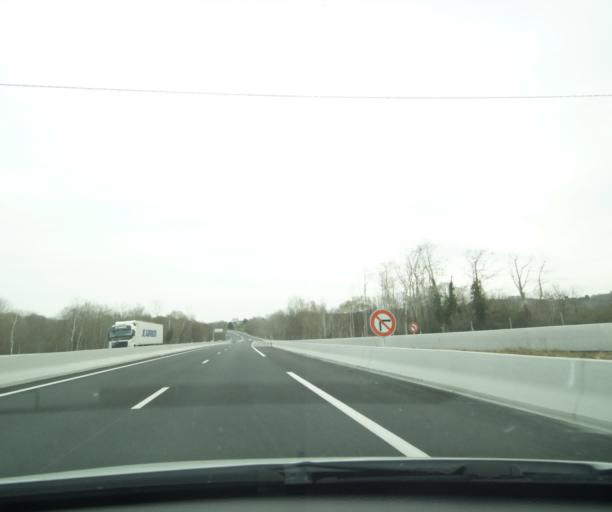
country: FR
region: Aquitaine
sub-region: Departement des Pyrenees-Atlantiques
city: Lahonce
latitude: 43.4505
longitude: -1.3804
